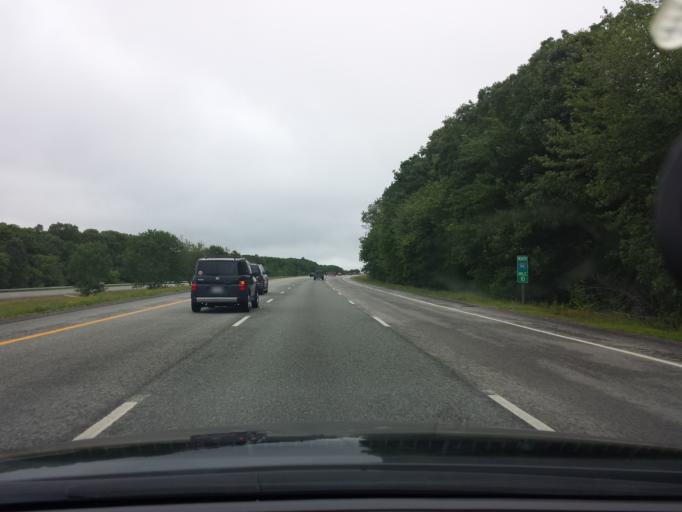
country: US
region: Rhode Island
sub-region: Washington County
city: Hope Valley
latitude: 41.5486
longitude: -71.6738
